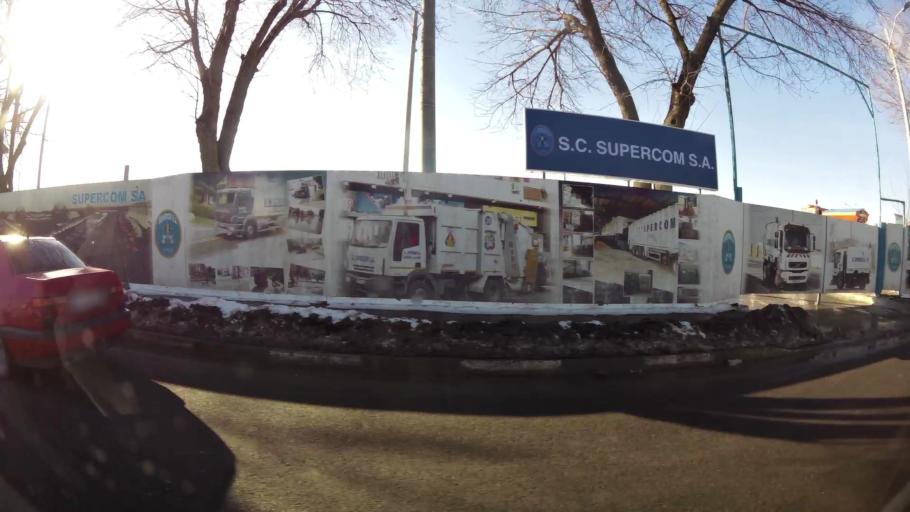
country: RO
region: Ilfov
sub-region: Comuna Fundeni-Dobroesti
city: Fundeni
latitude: 44.4741
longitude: 26.1410
